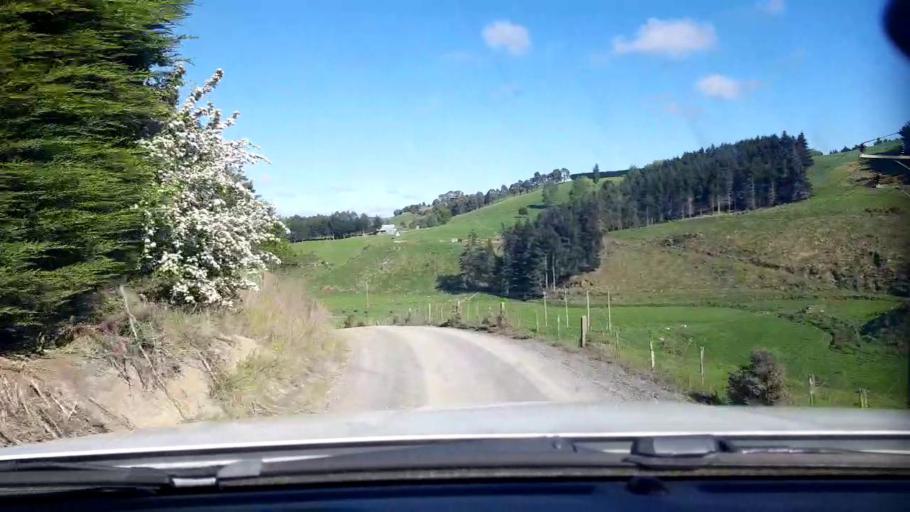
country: NZ
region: Otago
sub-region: Clutha District
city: Balclutha
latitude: -46.2231
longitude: 169.7430
